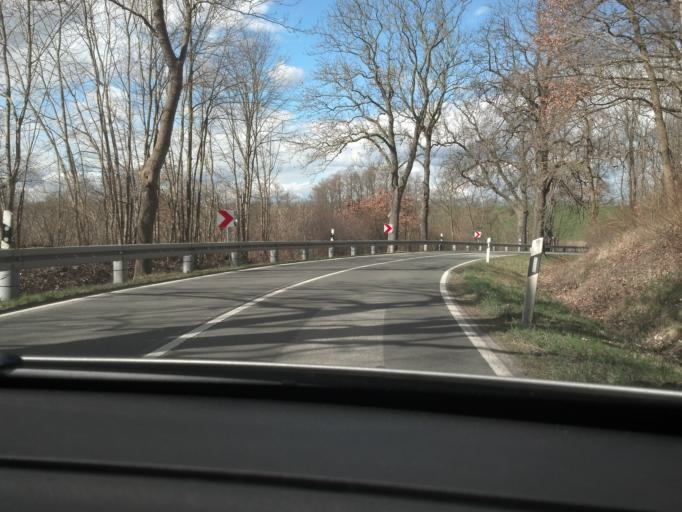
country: DE
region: Mecklenburg-Vorpommern
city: Loitz
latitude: 53.4011
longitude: 13.3628
